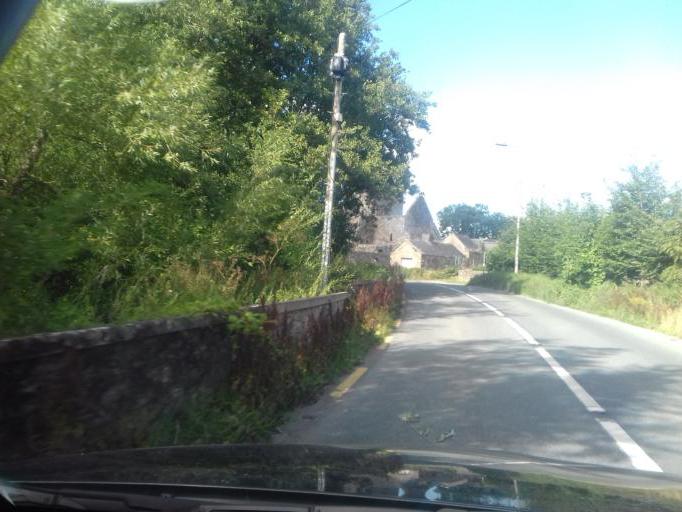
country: IE
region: Leinster
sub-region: Kilkenny
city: Thomastown
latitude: 52.5099
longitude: -7.1585
